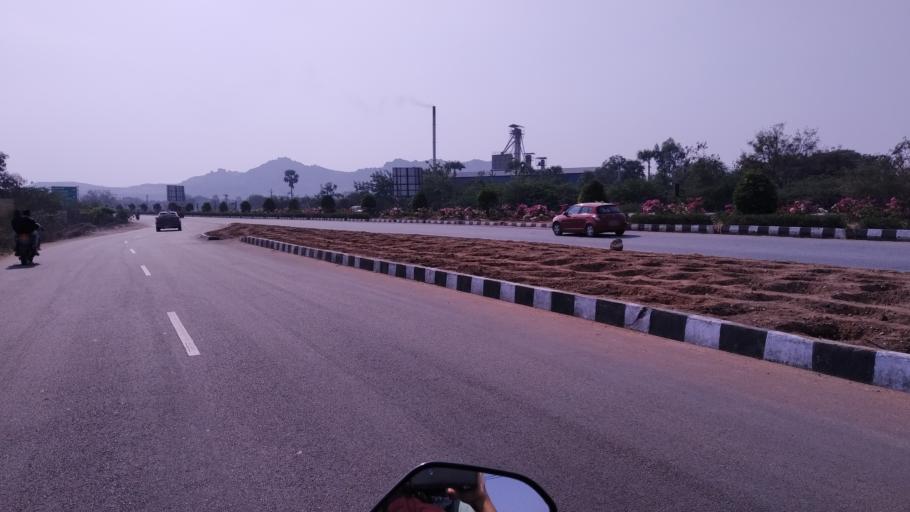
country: IN
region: Telangana
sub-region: Nalgonda
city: Bhongir
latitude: 17.5344
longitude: 78.9307
